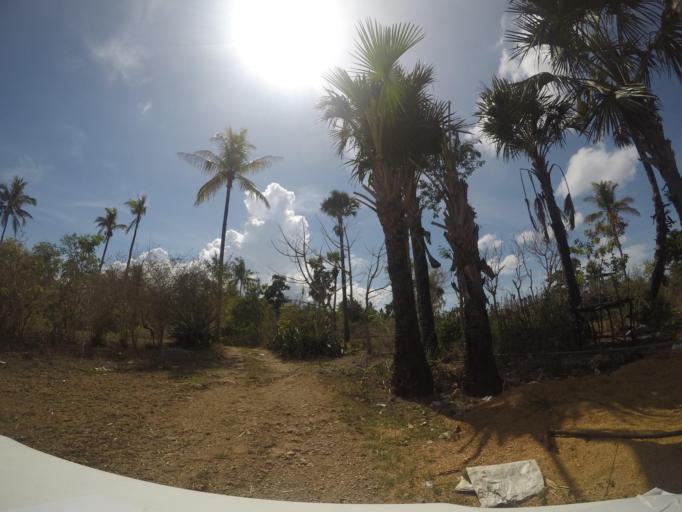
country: TL
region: Baucau
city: Baucau
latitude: -8.4669
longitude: 126.4626
